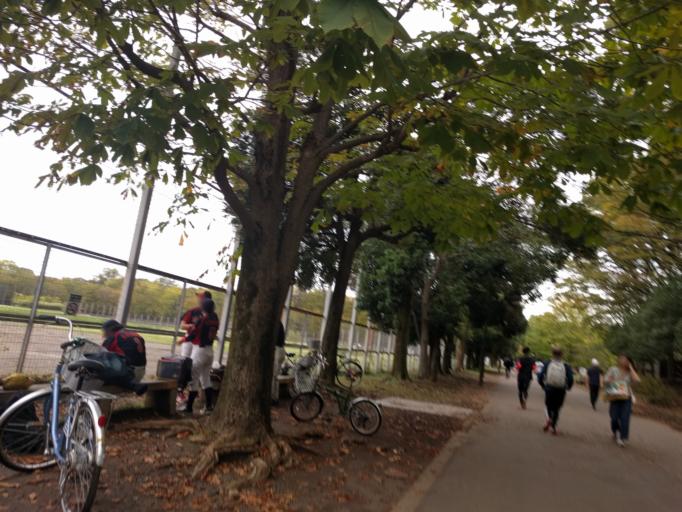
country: JP
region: Saitama
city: Wako
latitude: 35.7658
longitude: 139.6322
